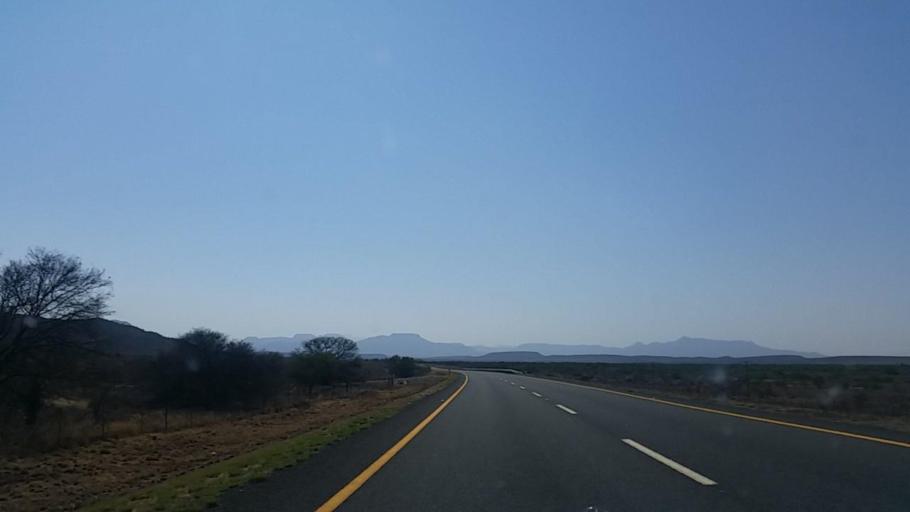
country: ZA
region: Eastern Cape
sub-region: Cacadu District Municipality
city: Graaff-Reinet
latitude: -32.3425
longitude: 24.4084
